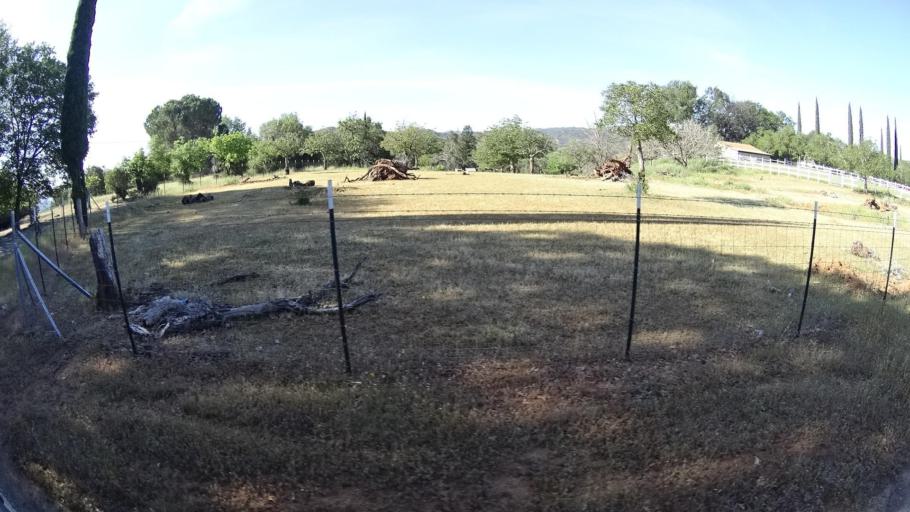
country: US
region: California
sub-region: Lake County
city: Lakeport
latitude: 39.0441
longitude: -122.9510
